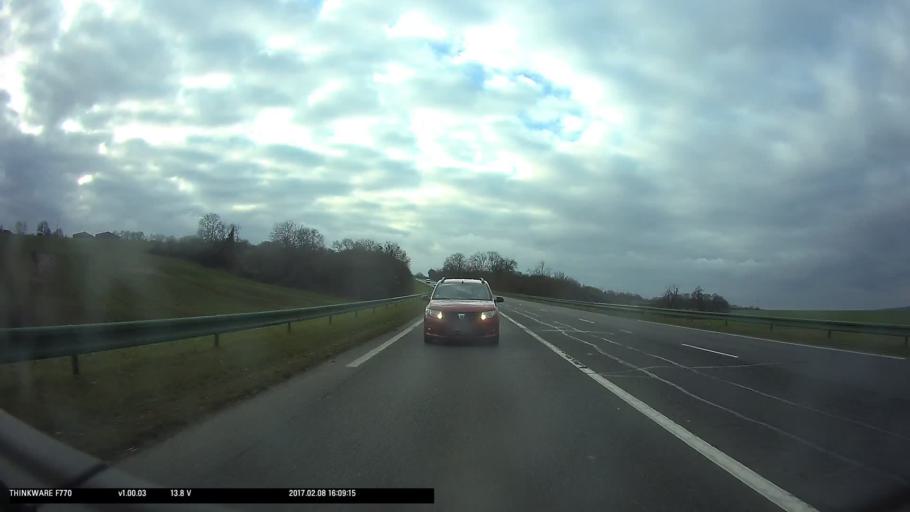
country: FR
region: Ile-de-France
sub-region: Departement du Val-d'Oise
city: Marines
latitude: 49.1231
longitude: 2.0159
